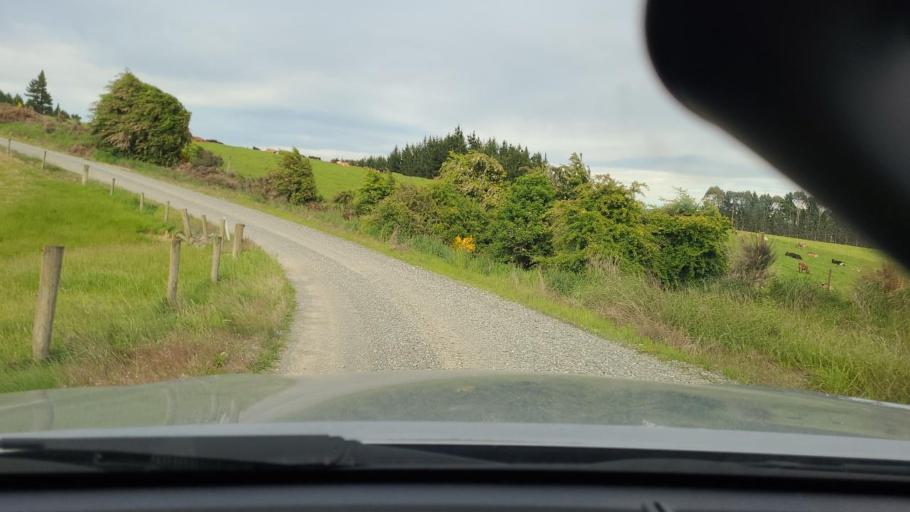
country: NZ
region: Southland
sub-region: Southland District
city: Winton
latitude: -45.6992
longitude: 168.1905
